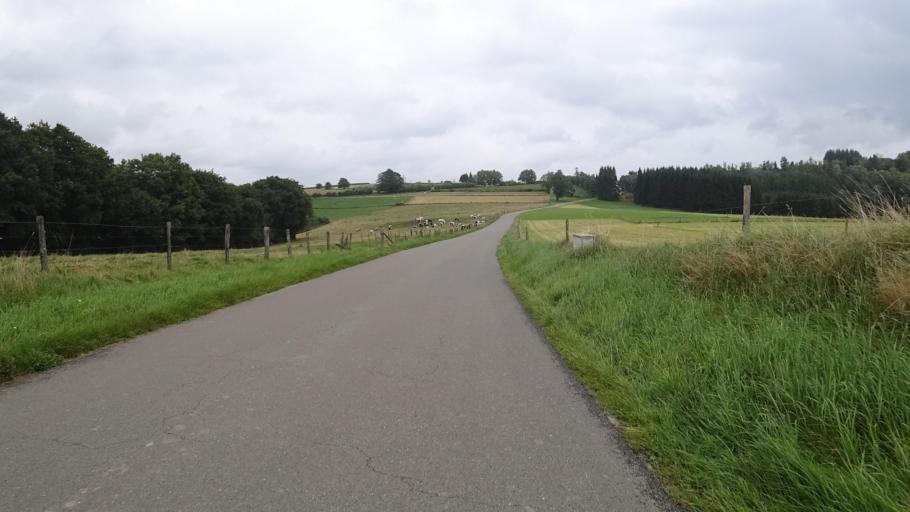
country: BE
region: Wallonia
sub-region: Province du Luxembourg
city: Chiny
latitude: 49.8035
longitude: 5.3680
